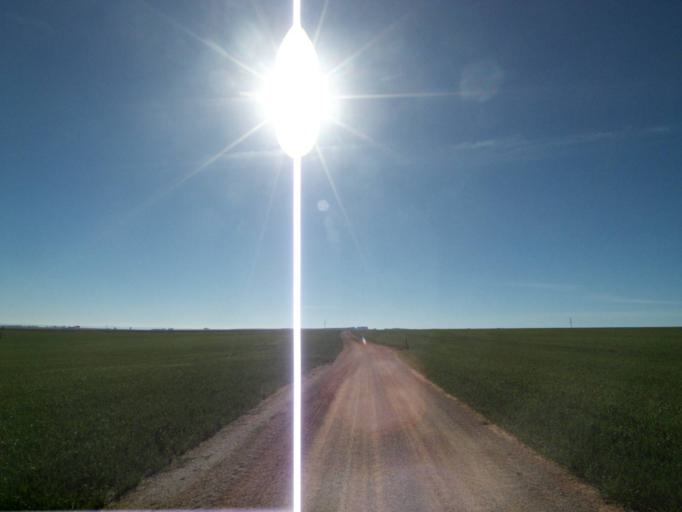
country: BR
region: Parana
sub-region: Tibagi
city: Tibagi
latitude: -24.5408
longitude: -50.3050
